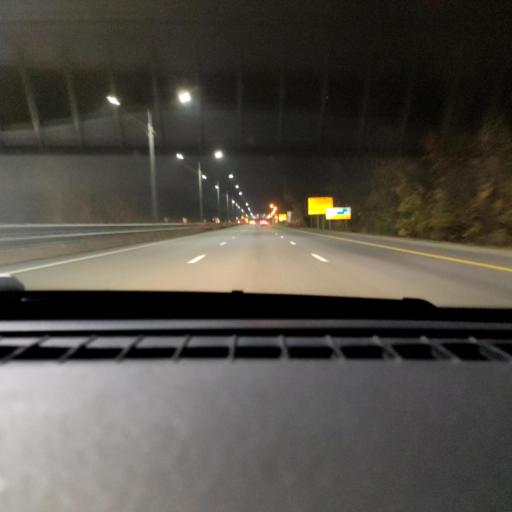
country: RU
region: Voronezj
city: Podgornoye
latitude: 51.8111
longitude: 39.2061
